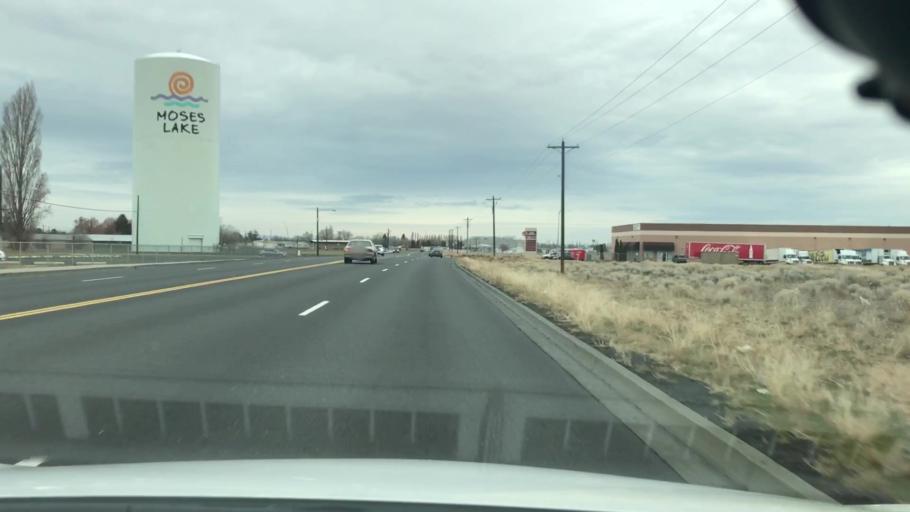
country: US
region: Washington
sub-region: Grant County
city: Moses Lake North
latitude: 47.1698
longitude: -119.3168
